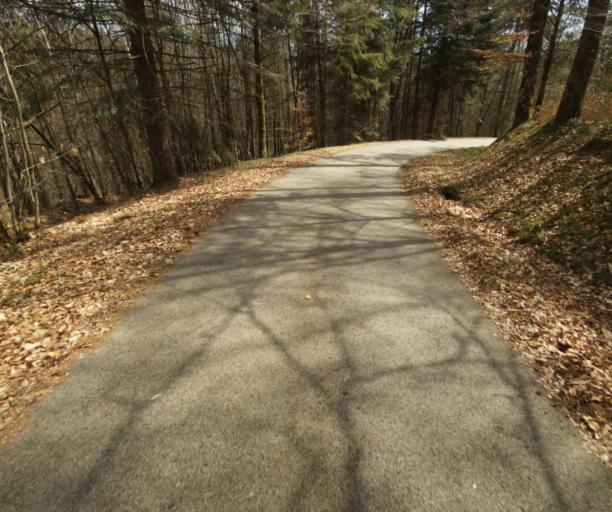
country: FR
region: Limousin
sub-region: Departement de la Correze
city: Naves
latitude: 45.3475
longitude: 1.8022
